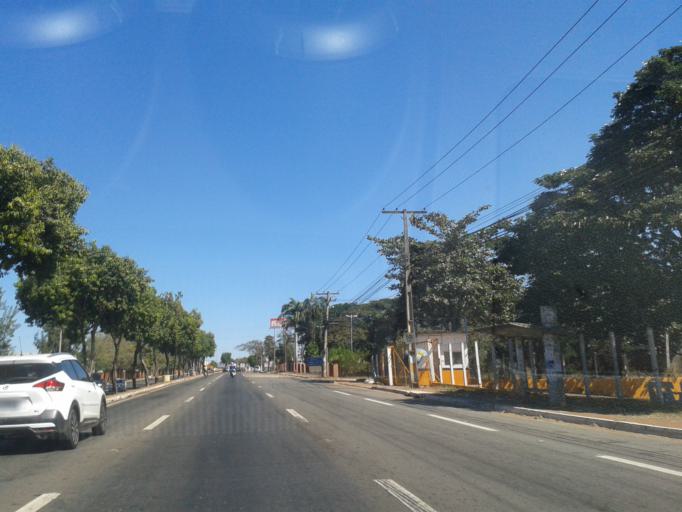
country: BR
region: Goias
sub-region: Goiania
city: Goiania
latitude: -16.6454
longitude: -49.3083
